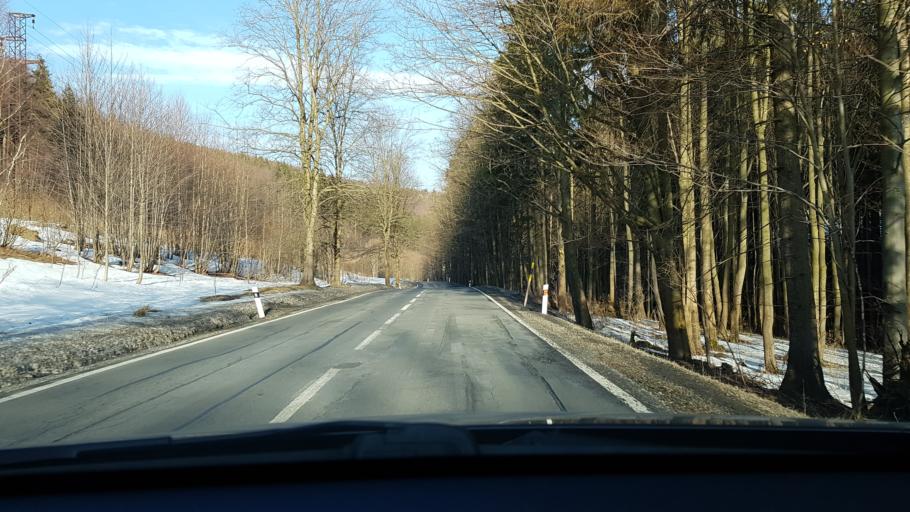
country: CZ
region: Olomoucky
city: Vapenna
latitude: 50.2030
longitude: 17.0719
